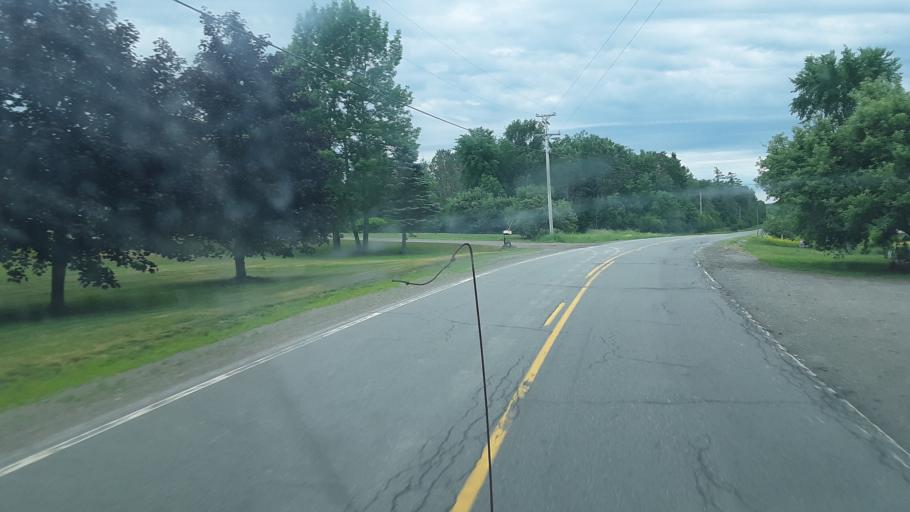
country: US
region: Maine
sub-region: Penobscot County
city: Patten
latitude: 45.8521
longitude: -68.3246
